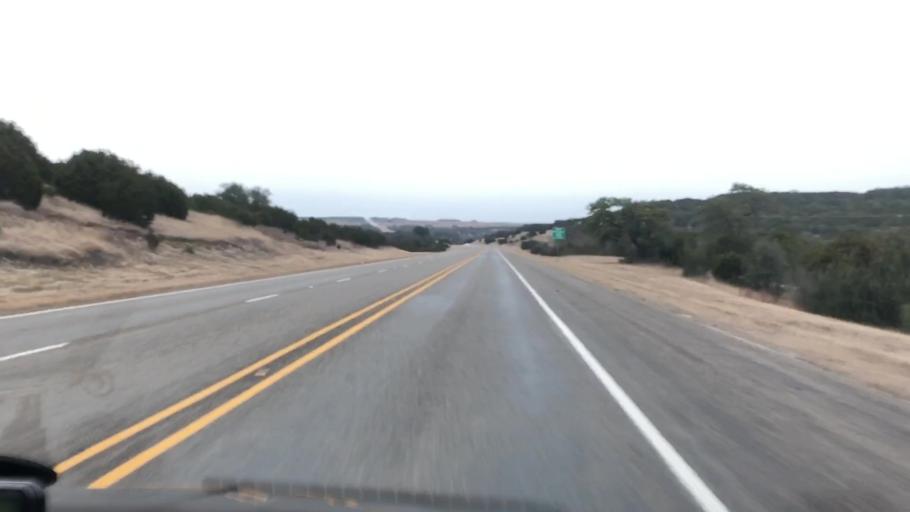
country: US
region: Texas
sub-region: Lampasas County
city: Lampasas
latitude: 31.2030
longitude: -98.1722
